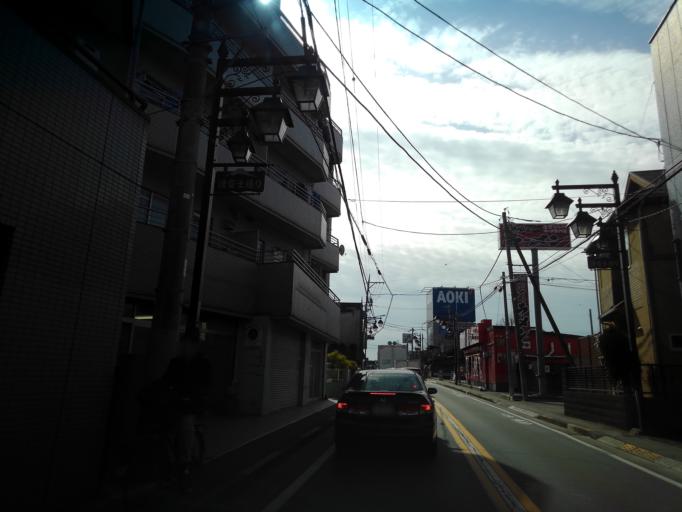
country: JP
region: Tokyo
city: Tanashicho
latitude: 35.7672
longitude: 139.5160
